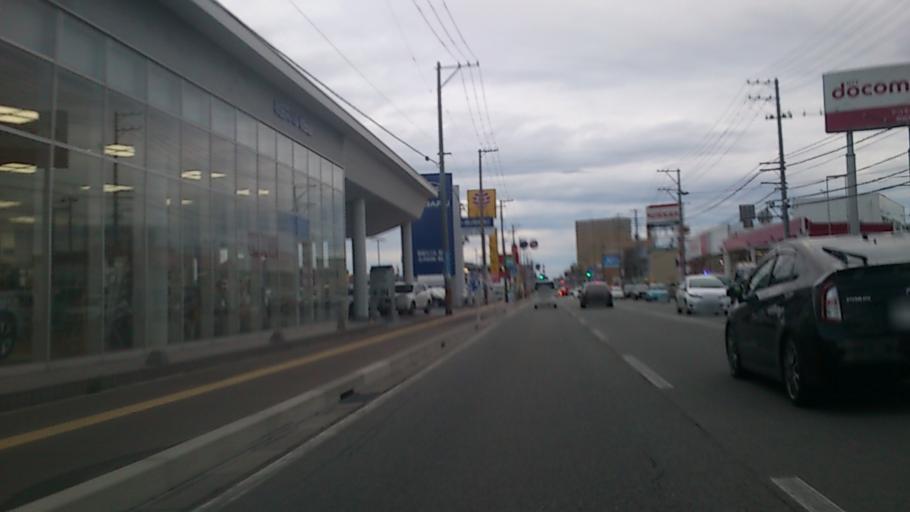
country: JP
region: Akita
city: Akita Shi
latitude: 39.7407
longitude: 140.0946
